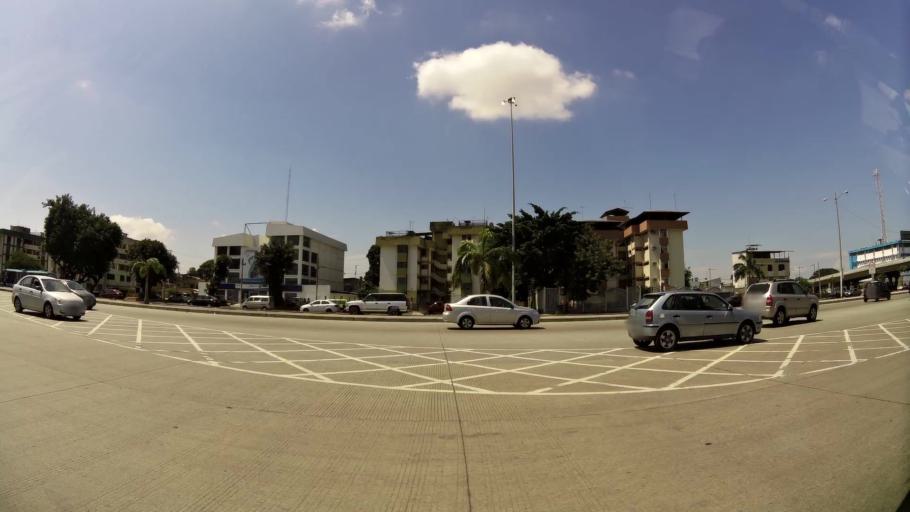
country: EC
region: Guayas
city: Guayaquil
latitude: -2.2380
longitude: -79.8967
